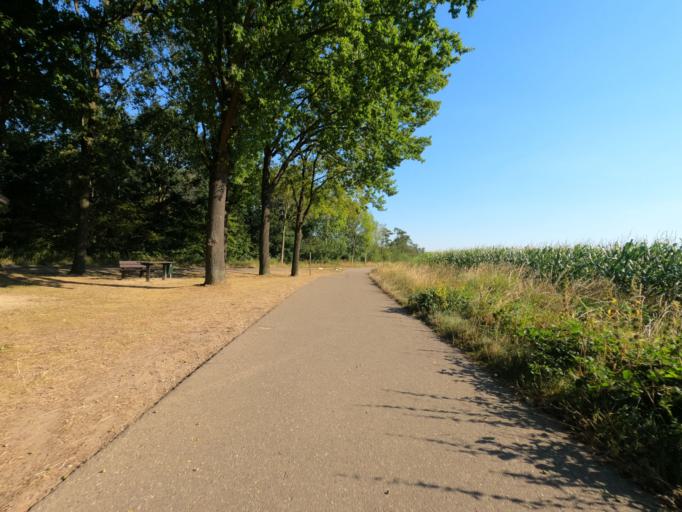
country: NL
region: Limburg
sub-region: Gemeente Roerdalen
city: Vlodrop
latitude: 51.1439
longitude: 6.0929
